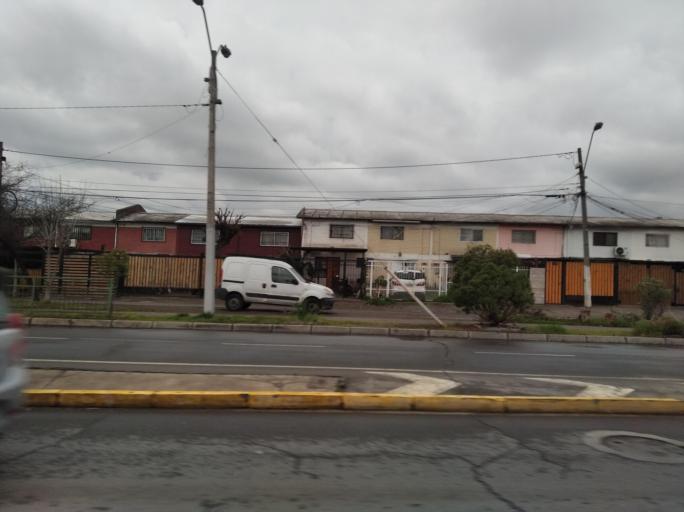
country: CL
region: Santiago Metropolitan
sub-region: Provincia de Santiago
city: Villa Presidente Frei, Nunoa, Santiago, Chile
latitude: -33.5153
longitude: -70.5907
